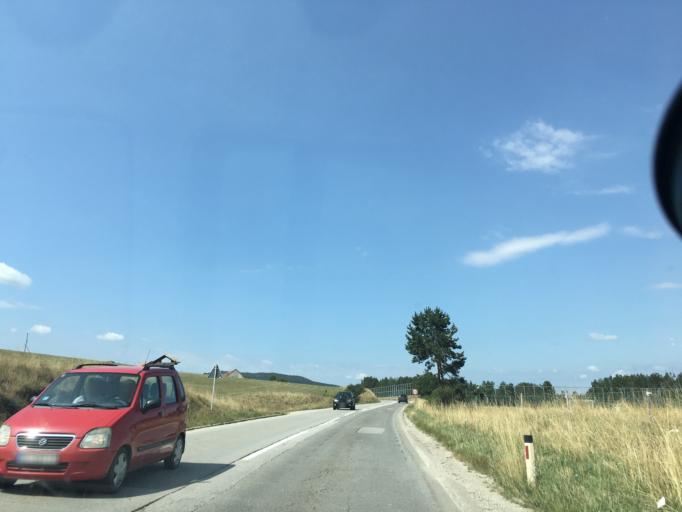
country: RS
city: Zlatibor
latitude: 43.7149
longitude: 19.6948
